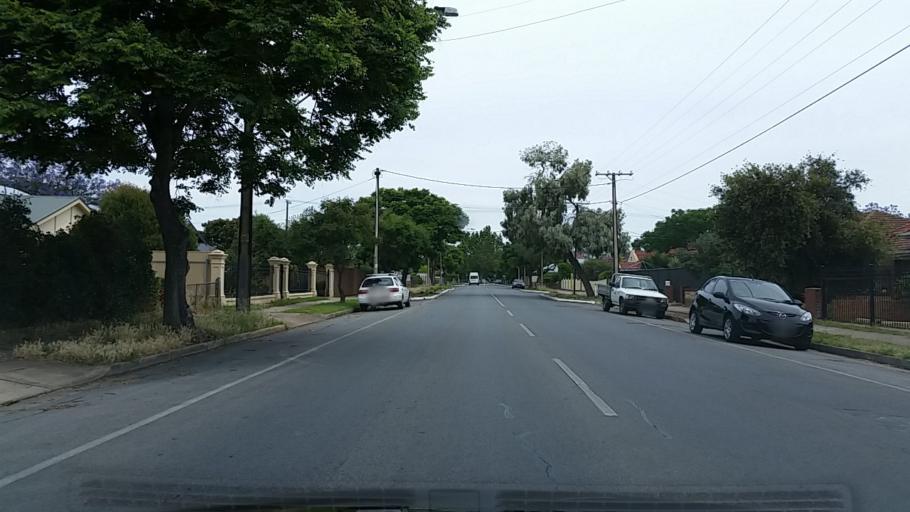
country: AU
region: South Australia
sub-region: Charles Sturt
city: Woodville
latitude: -34.8858
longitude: 138.5622
